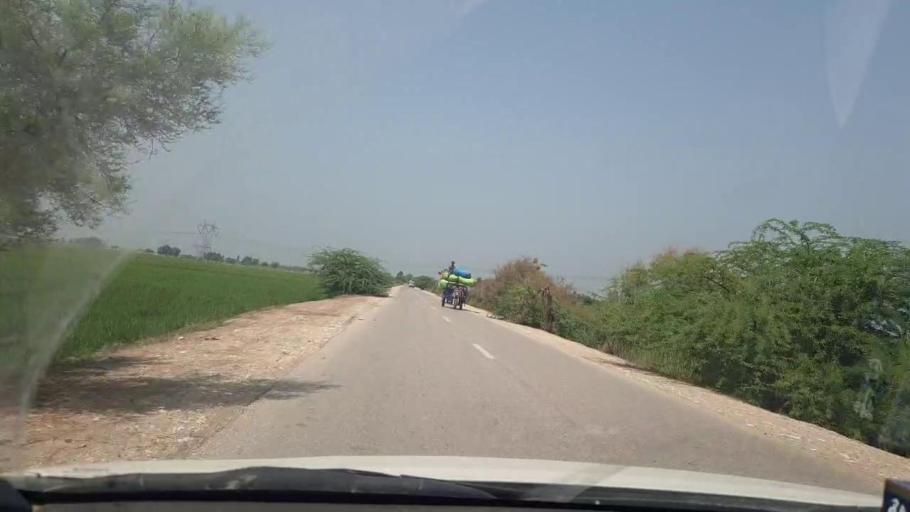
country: PK
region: Sindh
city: Rustam jo Goth
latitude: 27.9567
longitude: 68.7390
